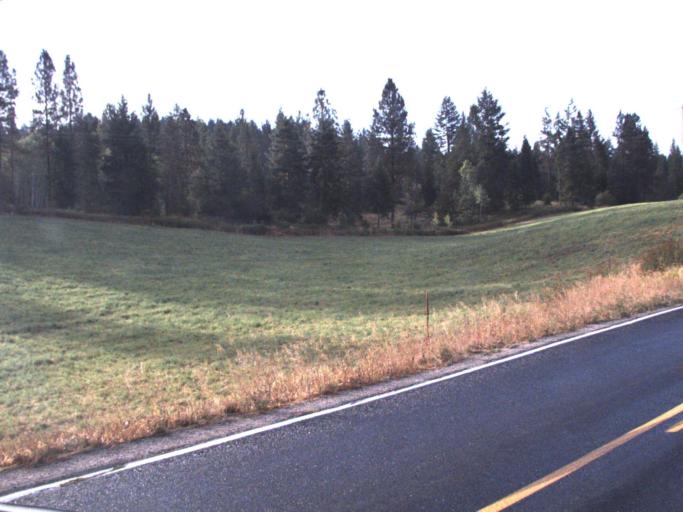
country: US
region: Washington
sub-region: Stevens County
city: Chewelah
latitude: 48.1116
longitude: -117.7556
